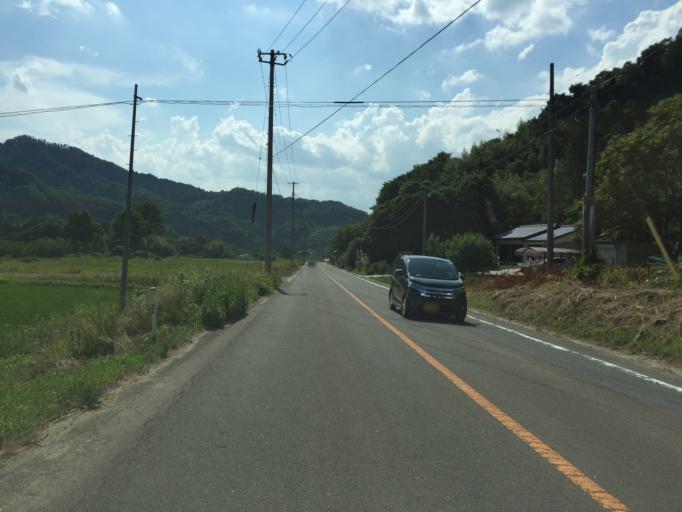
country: JP
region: Fukushima
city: Yanagawamachi-saiwaicho
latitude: 37.8054
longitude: 140.6256
